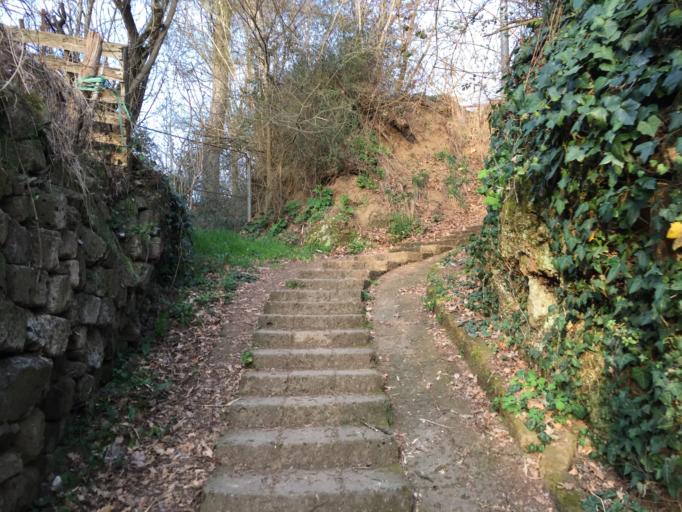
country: IT
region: Latium
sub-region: Provincia di Viterbo
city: Calcata Nuova
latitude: 42.2165
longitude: 12.4237
